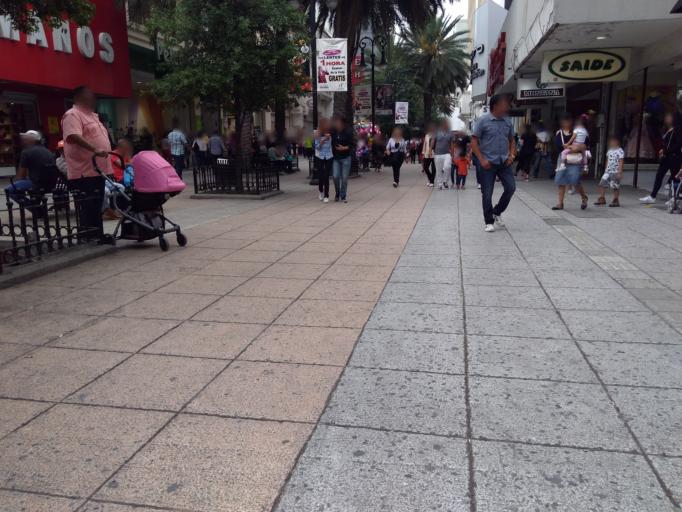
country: MX
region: Nuevo Leon
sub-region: Monterrey
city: Monterrey
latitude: 25.6675
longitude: -100.3142
